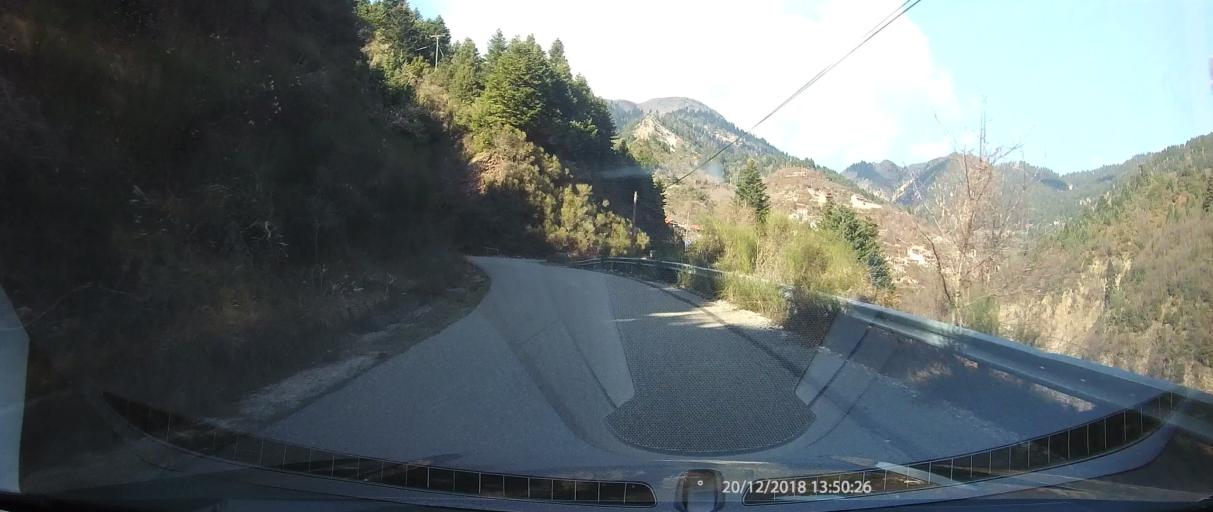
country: GR
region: West Greece
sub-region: Nomos Aitolias kai Akarnanias
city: Paravola
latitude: 38.6976
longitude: 21.6053
